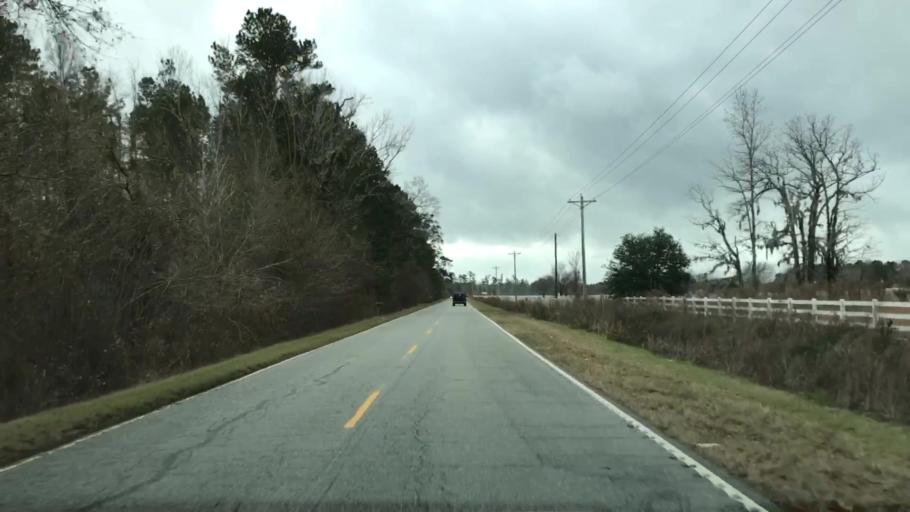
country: US
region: South Carolina
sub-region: Florence County
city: Johnsonville
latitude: 33.6564
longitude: -79.4192
